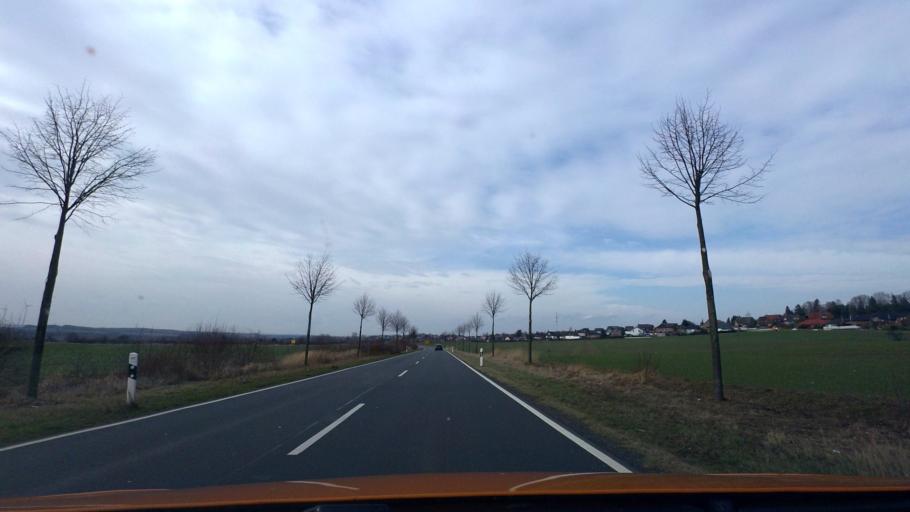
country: DE
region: Lower Saxony
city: Helmstedt
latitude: 52.2133
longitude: 11.0269
